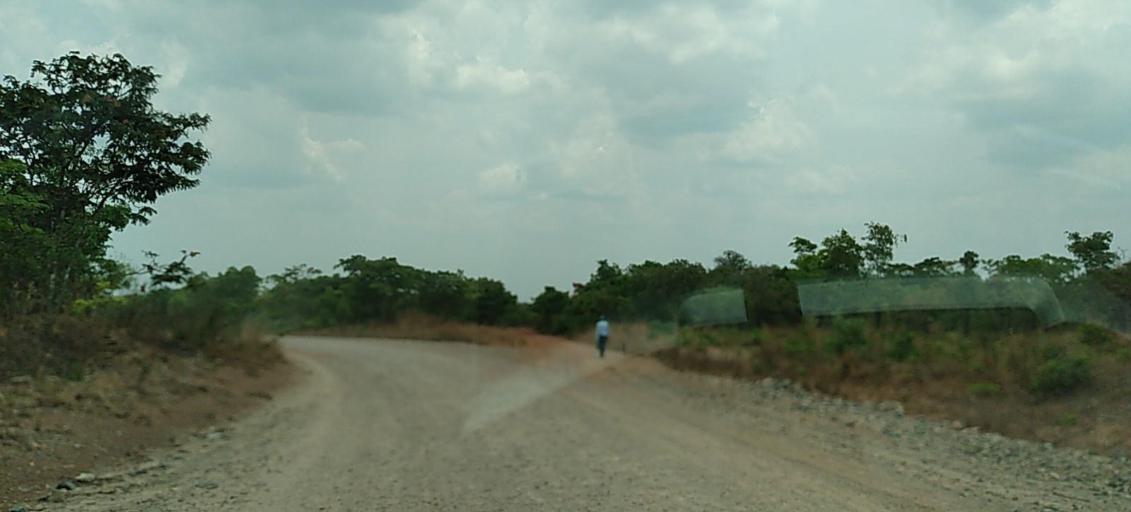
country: ZM
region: Copperbelt
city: Chililabombwe
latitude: -12.3102
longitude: 27.7911
